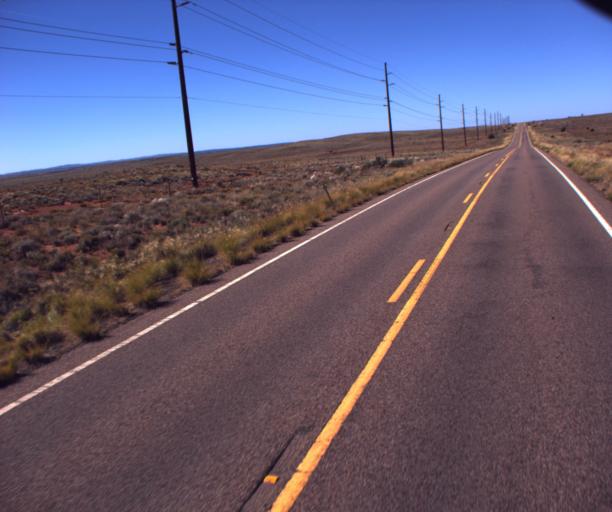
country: US
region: Arizona
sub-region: Navajo County
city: Taylor
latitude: 34.4934
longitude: -110.2150
